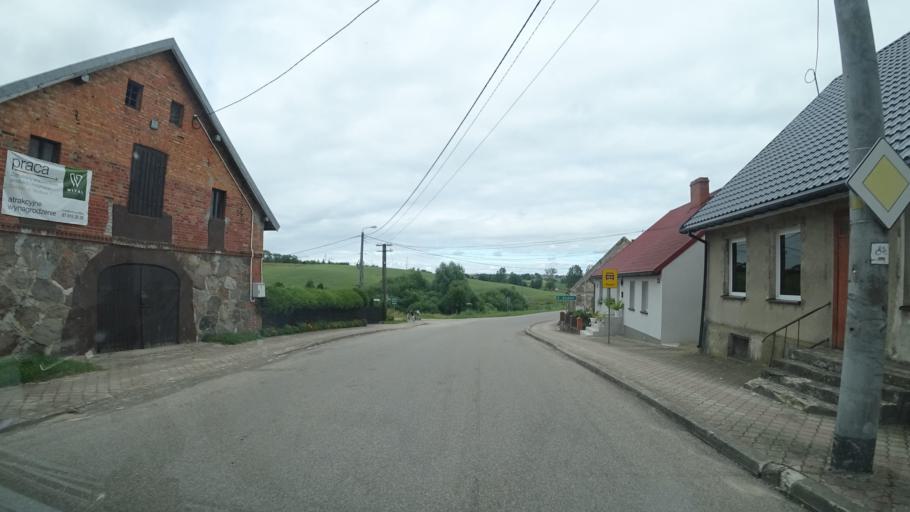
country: PL
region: Podlasie
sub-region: Powiat suwalski
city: Filipow
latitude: 54.2885
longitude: 22.5584
